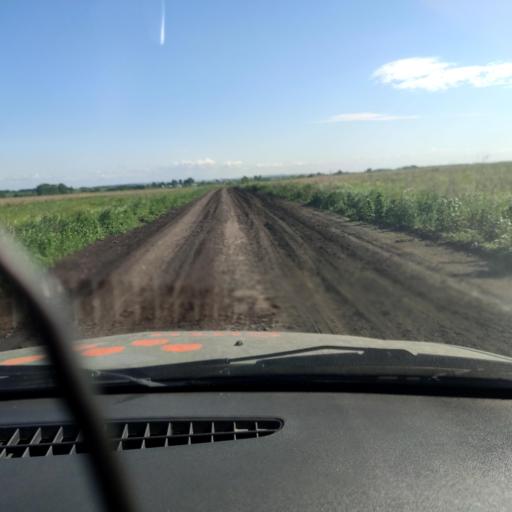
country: RU
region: Bashkortostan
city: Avdon
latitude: 54.5654
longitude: 55.8309
